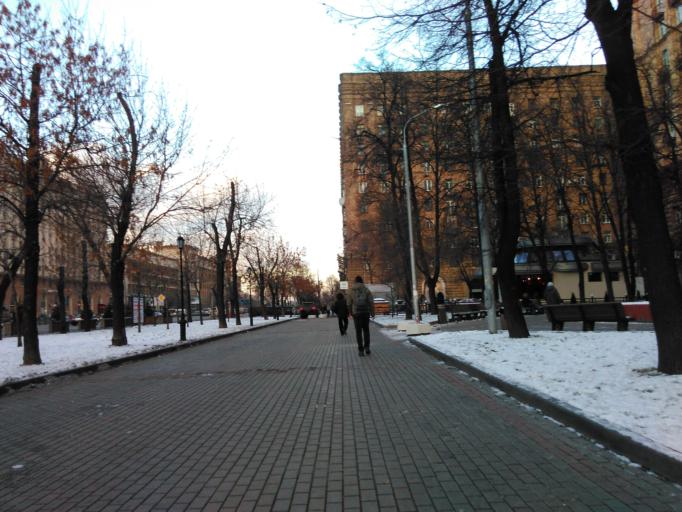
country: RU
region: Moscow
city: Mar'ina Roshcha
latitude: 55.8116
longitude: 37.6384
